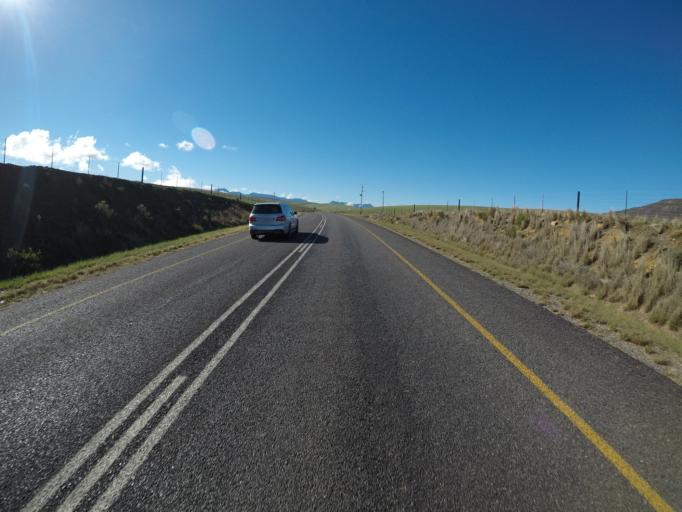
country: ZA
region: Western Cape
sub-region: Overberg District Municipality
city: Caledon
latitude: -34.1547
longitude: 19.4704
